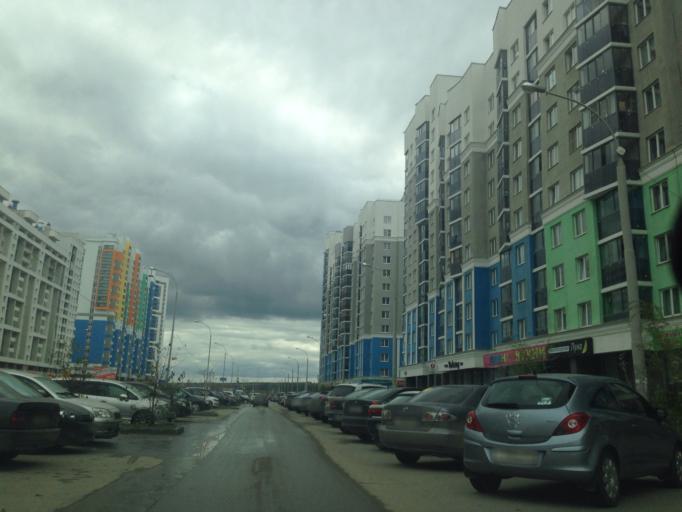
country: RU
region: Sverdlovsk
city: Shirokaya Rechka
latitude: 56.7913
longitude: 60.5177
